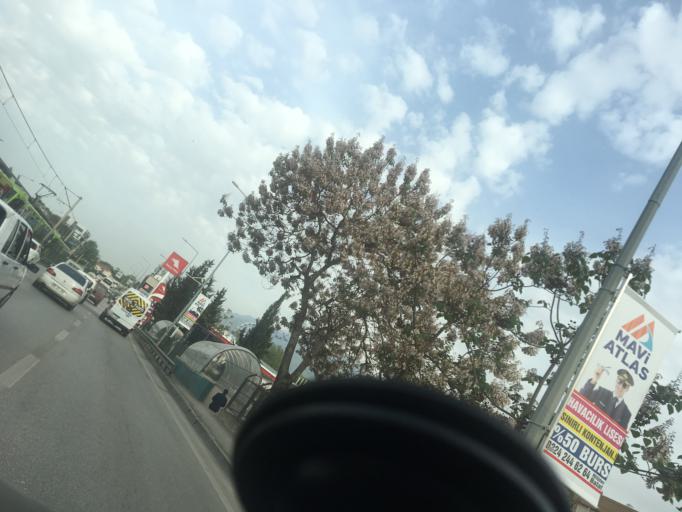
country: TR
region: Bursa
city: Yildirim
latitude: 40.2003
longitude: 29.0401
